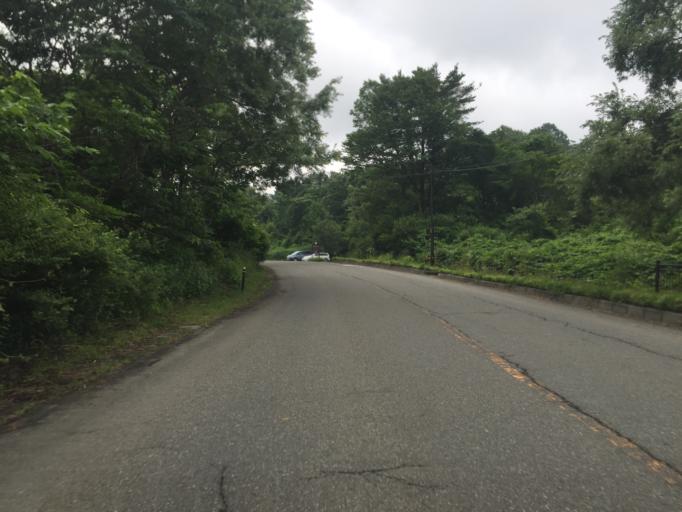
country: JP
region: Fukushima
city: Inawashiro
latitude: 37.6673
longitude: 140.0770
